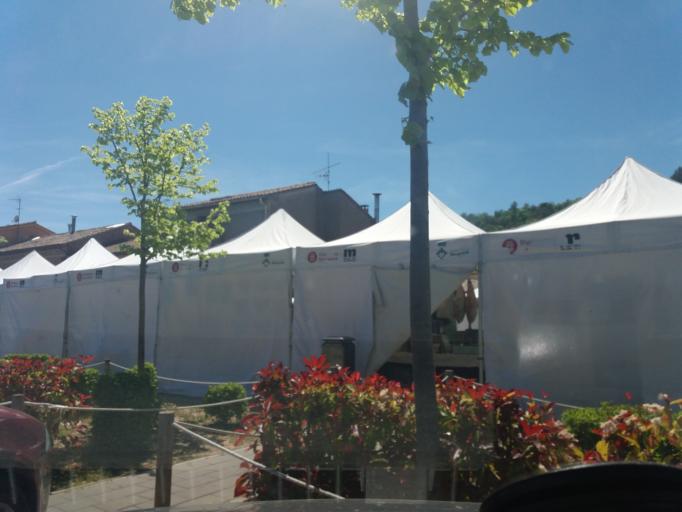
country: ES
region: Catalonia
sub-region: Provincia de Barcelona
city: Avia
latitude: 42.0712
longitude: 1.8700
